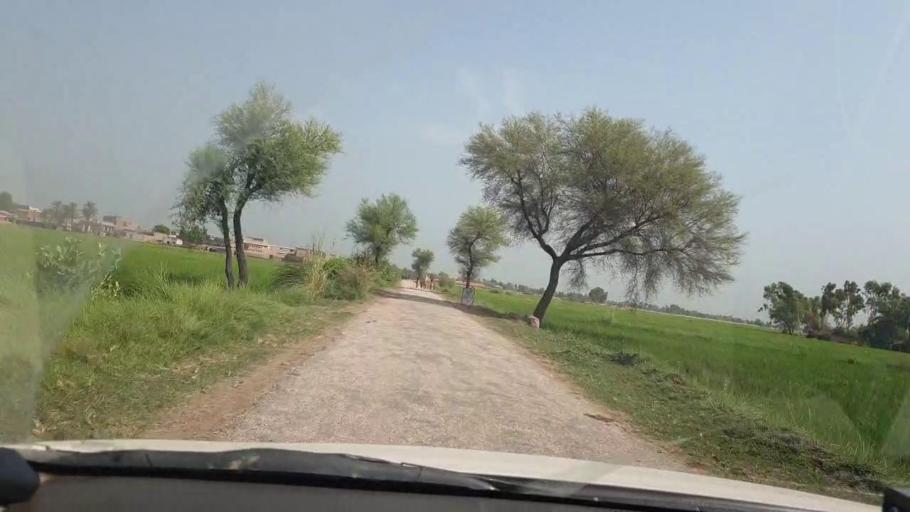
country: PK
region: Sindh
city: Chak
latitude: 27.8351
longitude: 68.7989
